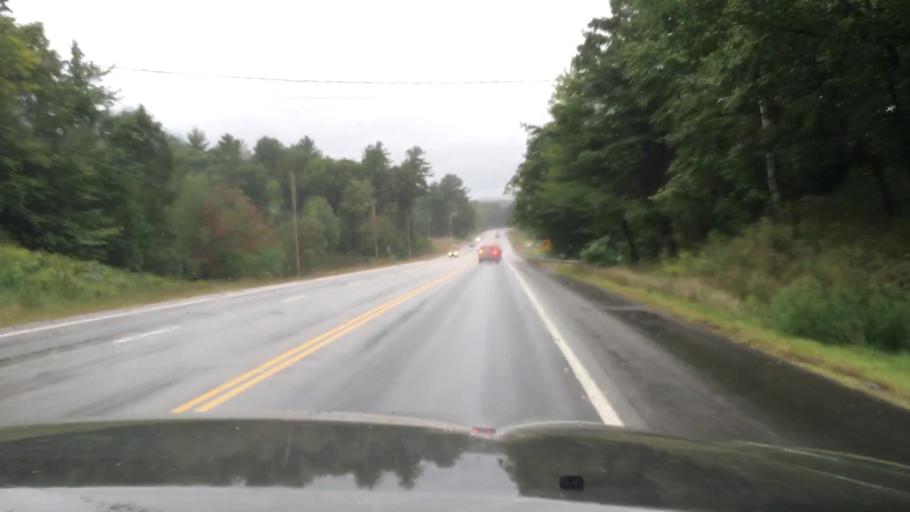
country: US
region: New Hampshire
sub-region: Cheshire County
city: Westmoreland
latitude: 42.9201
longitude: -72.3831
